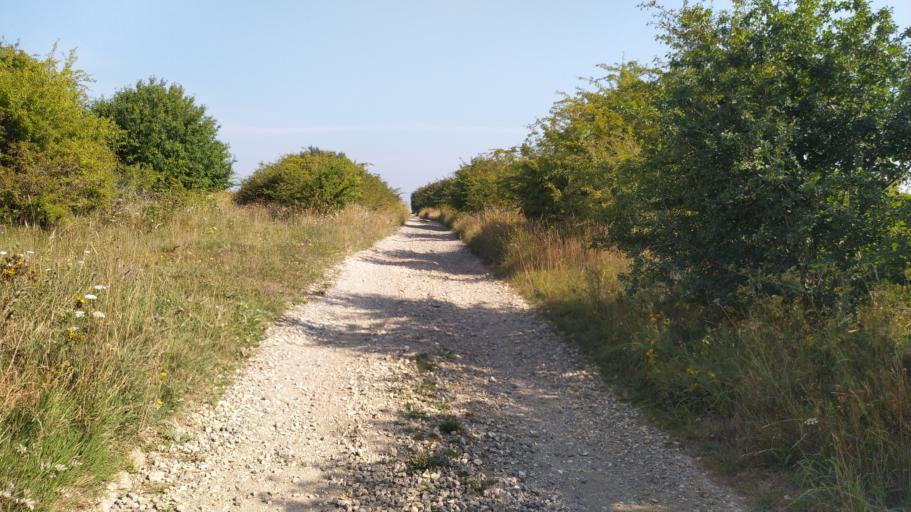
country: GB
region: England
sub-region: Wiltshire
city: Shrewton
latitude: 51.1702
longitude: -1.9522
